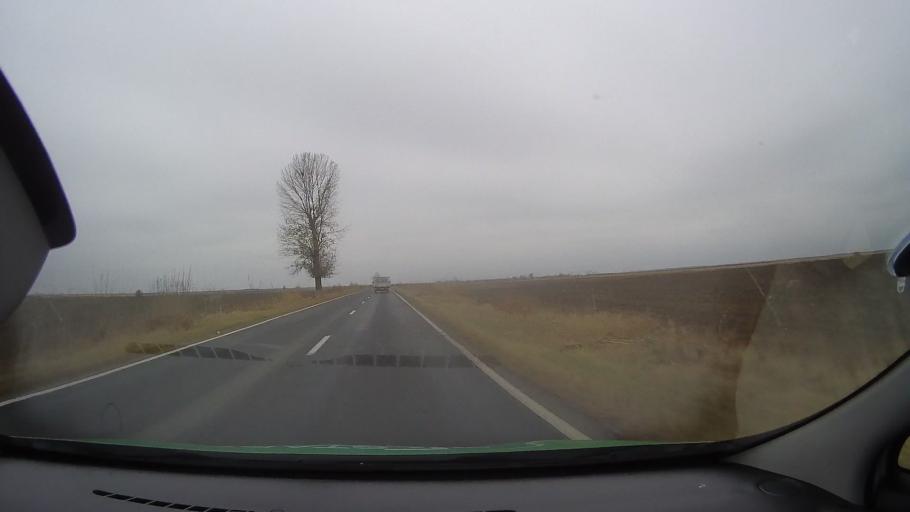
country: RO
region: Ialomita
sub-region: Comuna Scanteia
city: Scanteia
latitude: 44.7455
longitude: 27.4446
